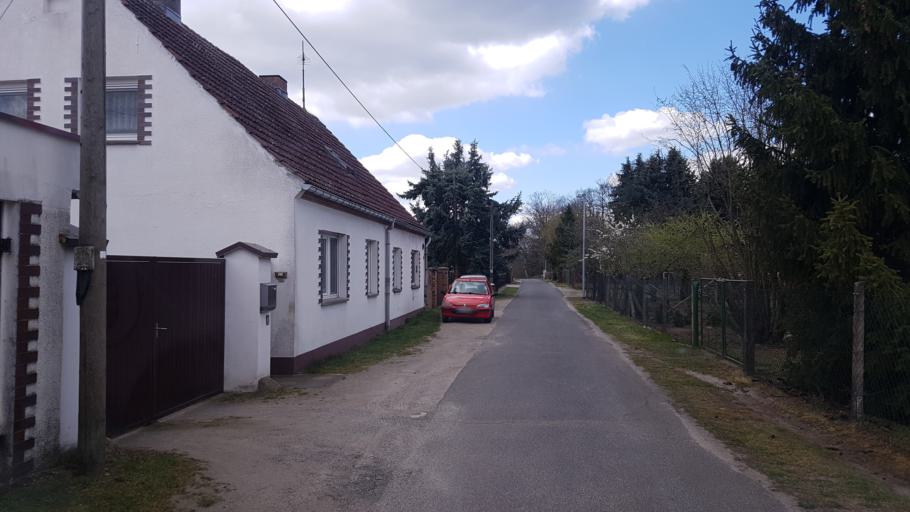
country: DE
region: Brandenburg
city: Sonnewalde
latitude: 51.6834
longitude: 13.6513
